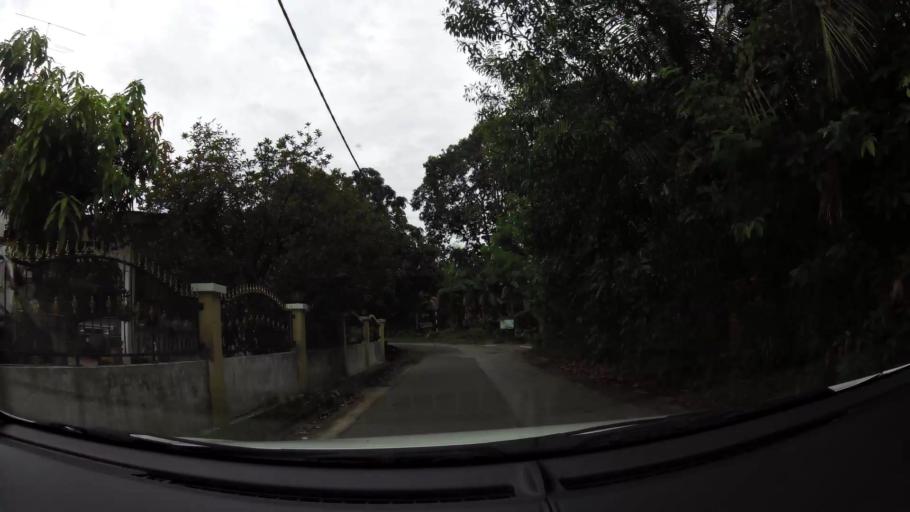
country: BN
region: Brunei and Muara
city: Bandar Seri Begawan
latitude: 4.8951
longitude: 114.9274
